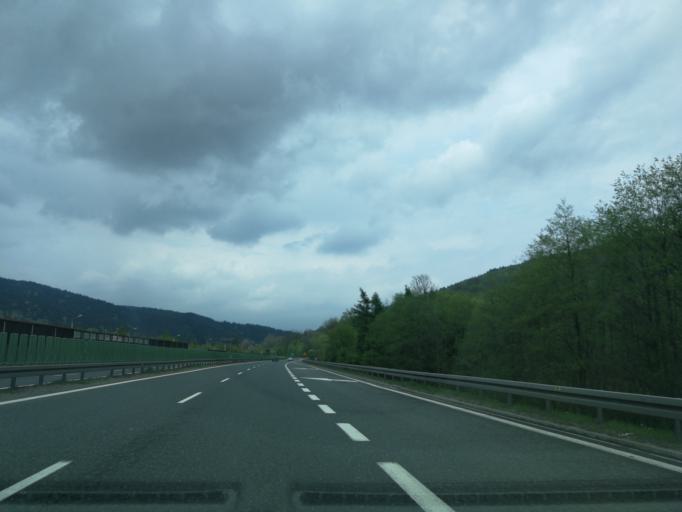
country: PL
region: Lesser Poland Voivodeship
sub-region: Powiat myslenicki
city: Stroza
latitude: 49.7997
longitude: 19.9245
